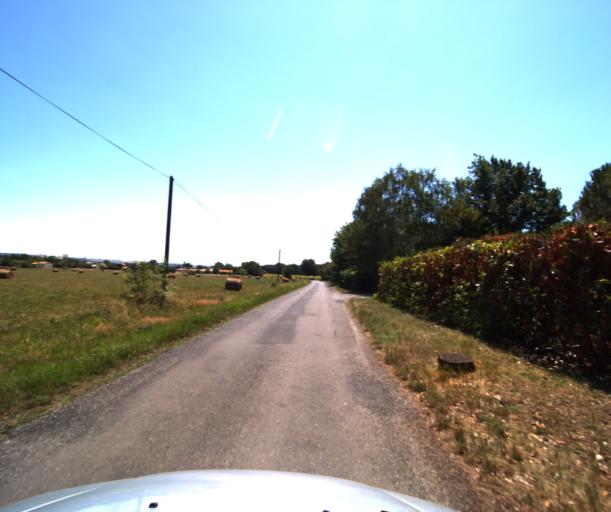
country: FR
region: Midi-Pyrenees
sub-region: Departement de la Haute-Garonne
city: Muret
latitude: 43.4544
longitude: 1.3461
